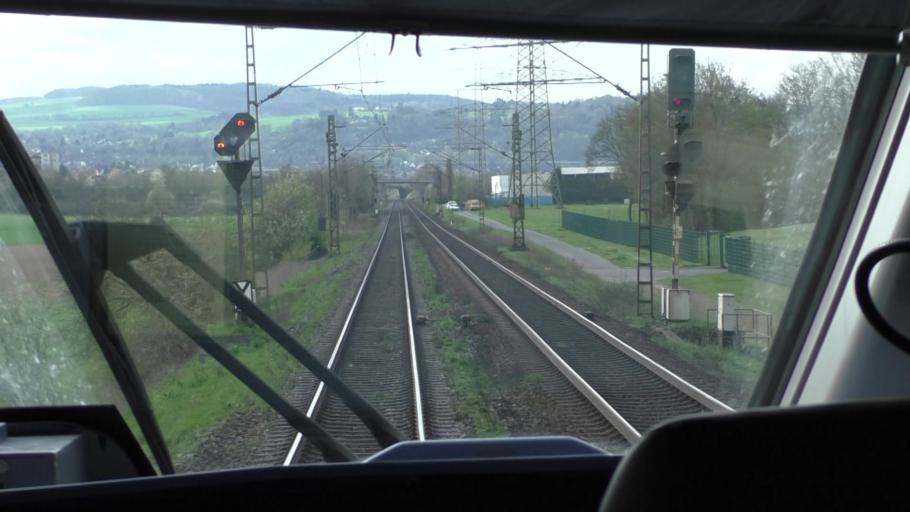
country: DE
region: Rheinland-Pfalz
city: Weissenthurm
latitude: 50.4273
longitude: 7.4347
